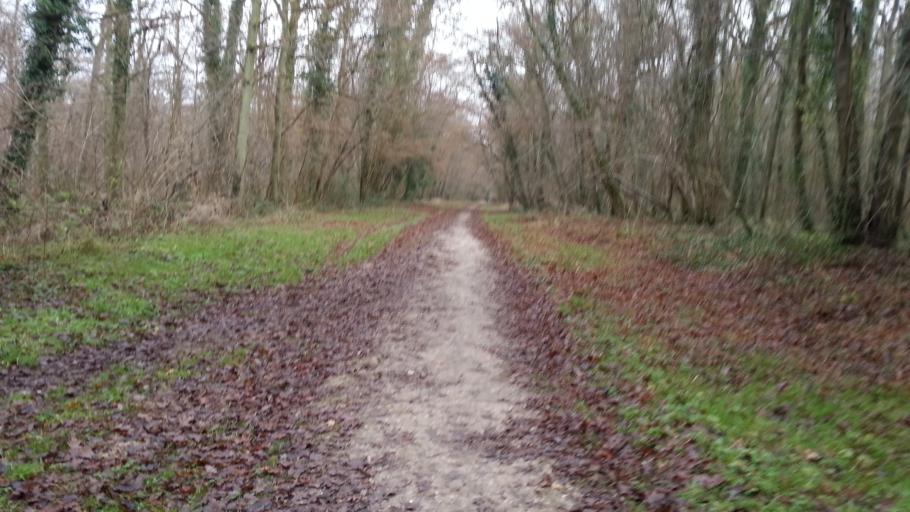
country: FR
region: Picardie
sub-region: Departement de l'Oise
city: Gouvieux
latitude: 49.1841
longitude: 2.3982
